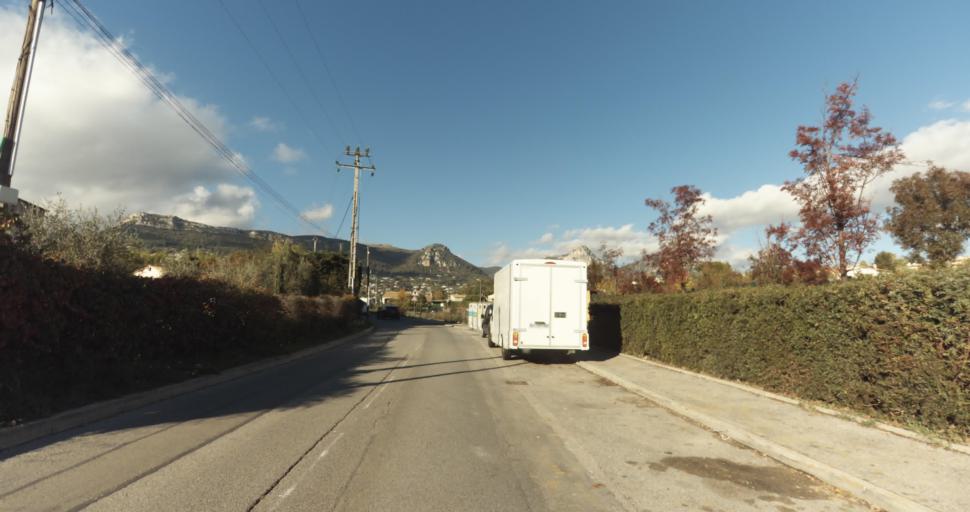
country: FR
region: Provence-Alpes-Cote d'Azur
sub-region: Departement des Alpes-Maritimes
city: Vence
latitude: 43.7166
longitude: 7.1299
